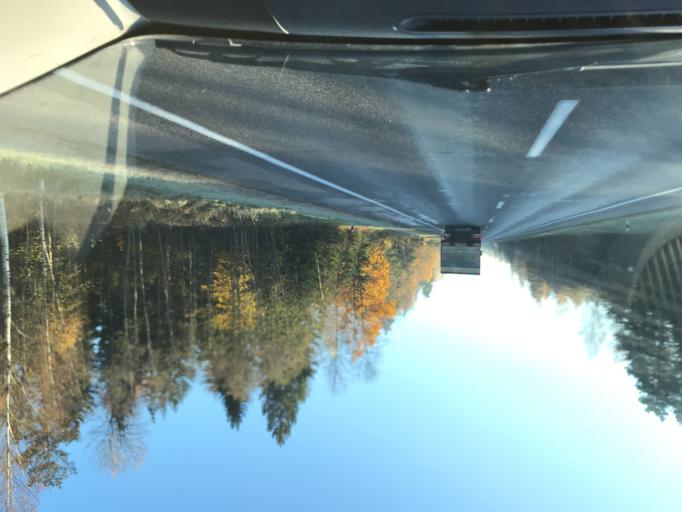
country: BY
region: Vitebsk
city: Vitebsk
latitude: 54.9471
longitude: 30.3624
